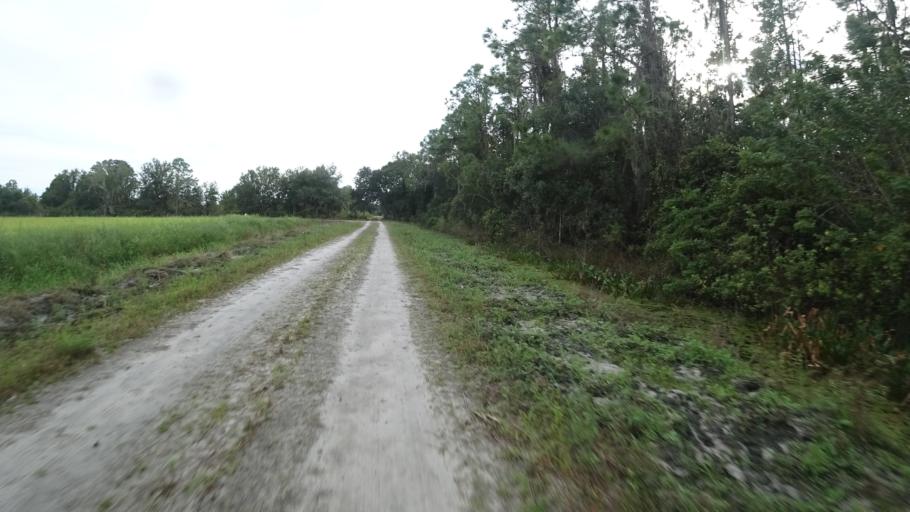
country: US
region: Florida
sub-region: Hillsborough County
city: Wimauma
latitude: 27.5599
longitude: -82.0820
